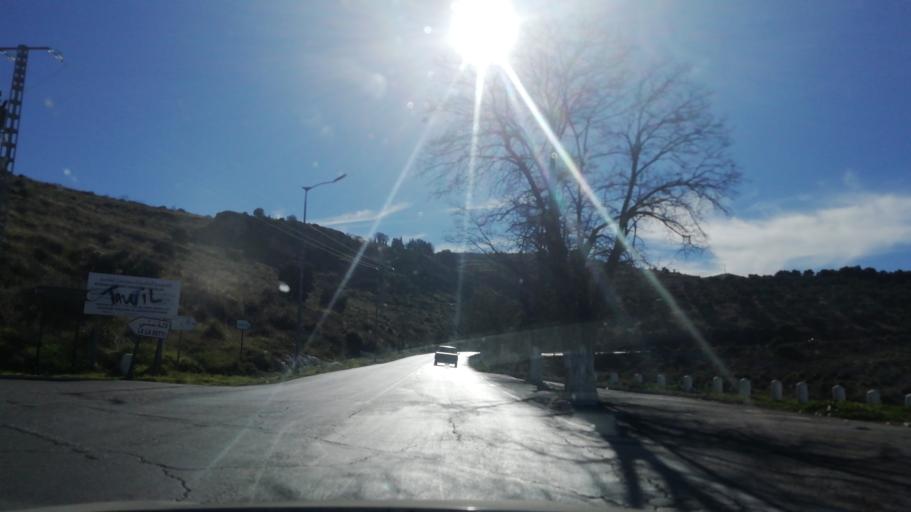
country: DZ
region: Tlemcen
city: Mansoura
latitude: 34.8549
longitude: -1.3472
